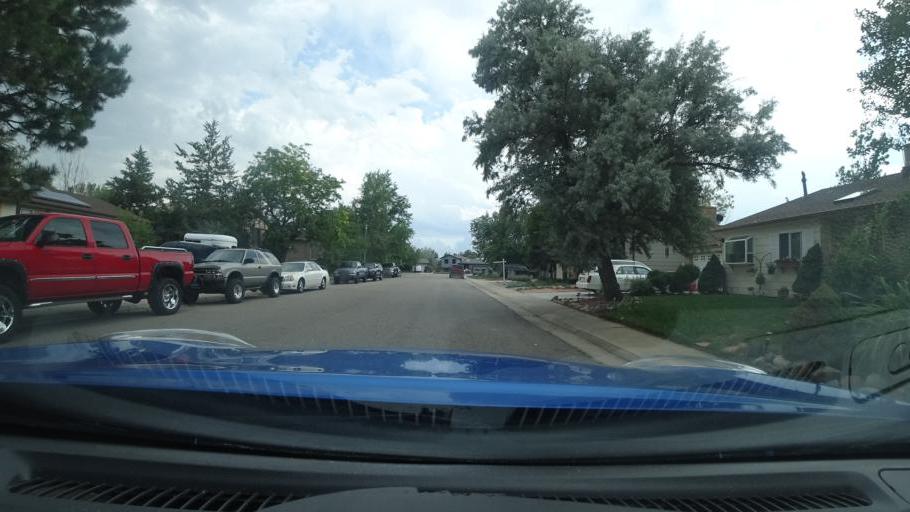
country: US
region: Colorado
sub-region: Adams County
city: Aurora
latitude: 39.6870
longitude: -104.7972
